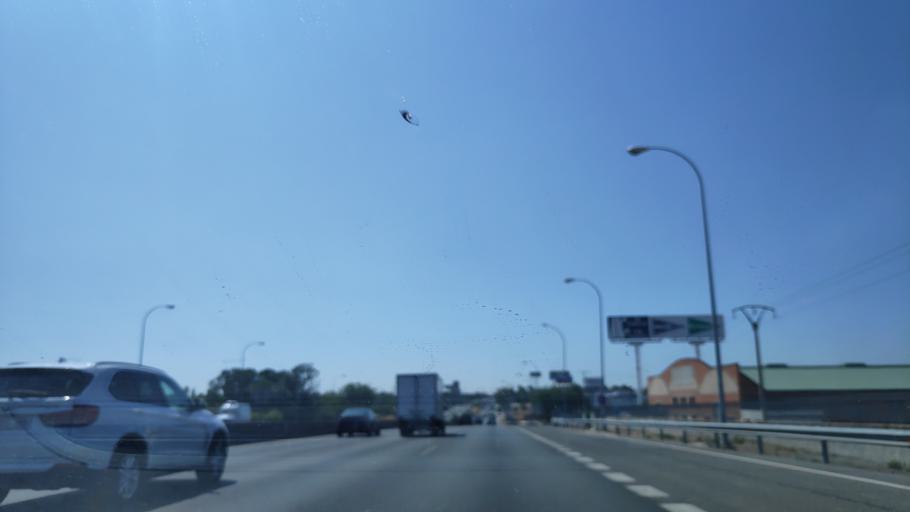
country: ES
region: Madrid
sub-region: Provincia de Madrid
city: Villaverde
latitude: 40.3554
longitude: -3.7221
